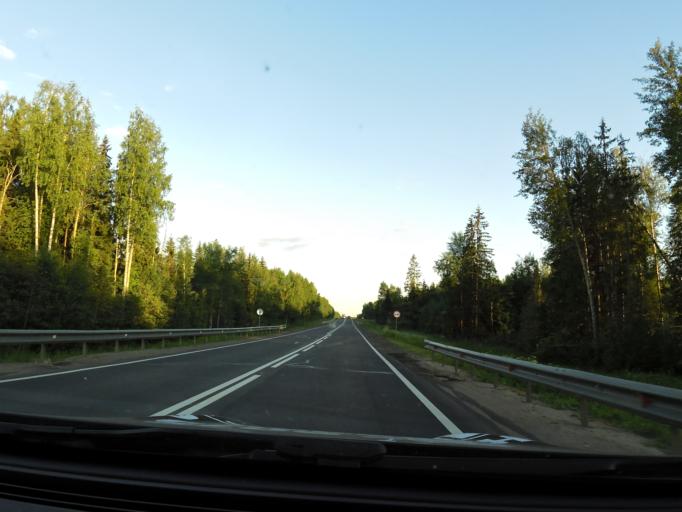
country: RU
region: Jaroslavl
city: Prechistoye
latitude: 58.5681
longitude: 40.3552
